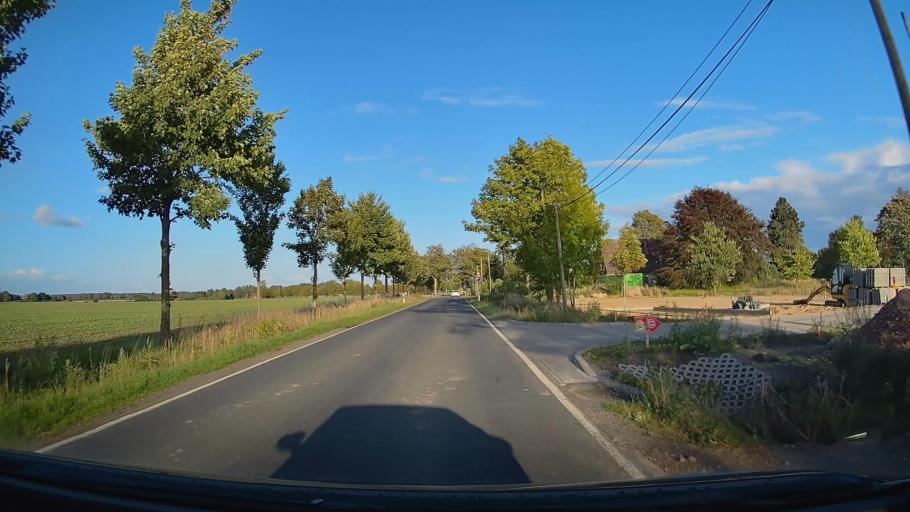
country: DE
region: Mecklenburg-Vorpommern
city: Steinhagen
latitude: 54.1883
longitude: 13.0040
